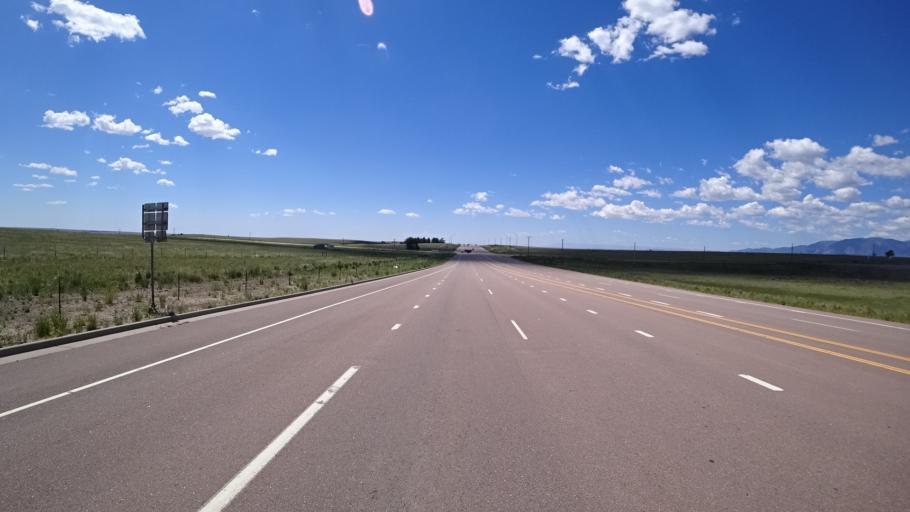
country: US
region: Colorado
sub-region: El Paso County
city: Cimarron Hills
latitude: 38.8403
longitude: -104.6828
